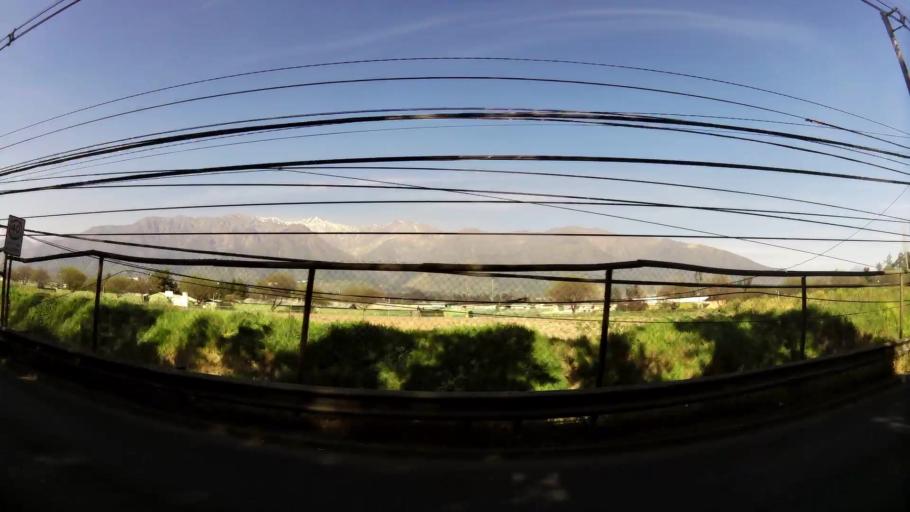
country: CL
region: Santiago Metropolitan
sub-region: Provincia de Santiago
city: Villa Presidente Frei, Nunoa, Santiago, Chile
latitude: -33.4976
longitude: -70.5601
